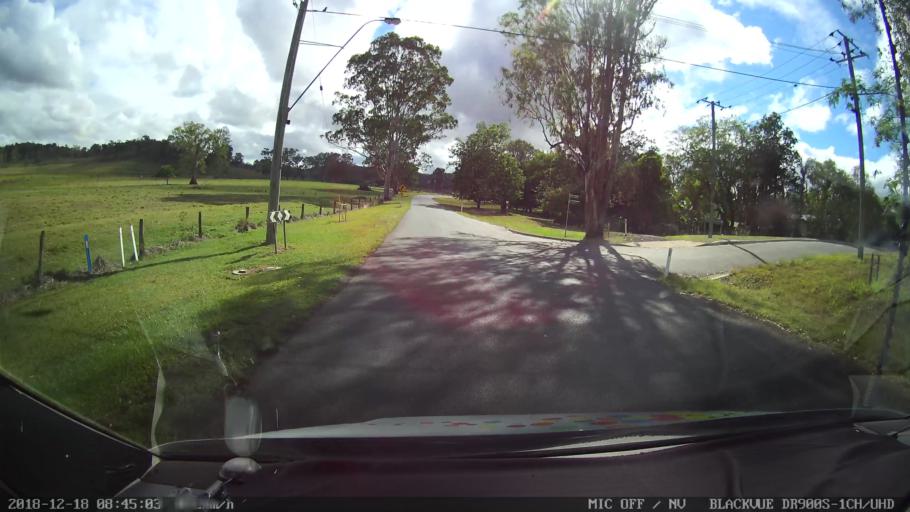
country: AU
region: Queensland
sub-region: Logan
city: Cedar Vale
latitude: -28.2110
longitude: 152.8658
